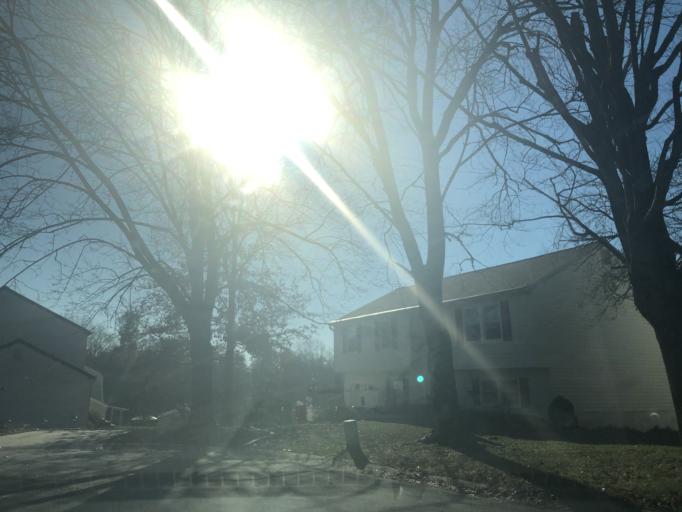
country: US
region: Maryland
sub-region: Howard County
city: Riverside
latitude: 39.1955
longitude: -76.8463
